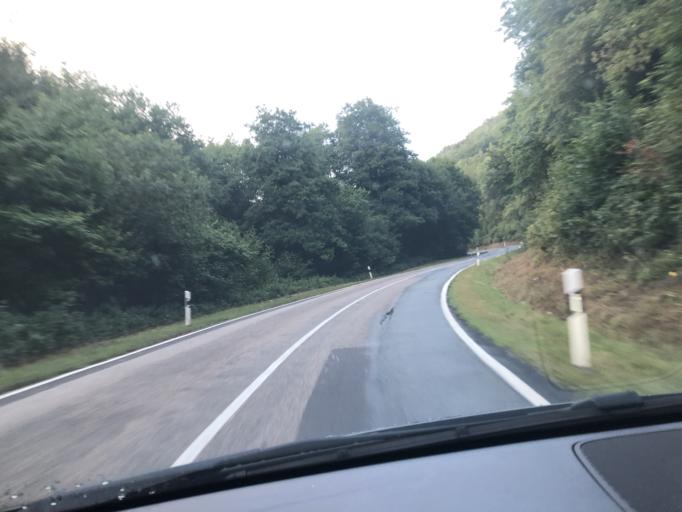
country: DE
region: Rheinland-Pfalz
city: Grimburg
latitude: 49.5942
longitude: 6.8736
